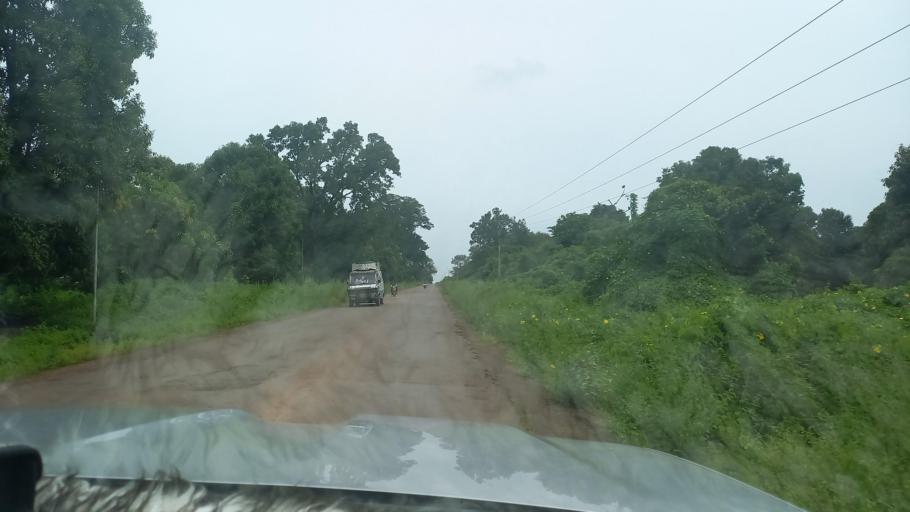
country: SN
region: Ziguinchor
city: Bignona
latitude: 12.8254
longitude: -16.1725
